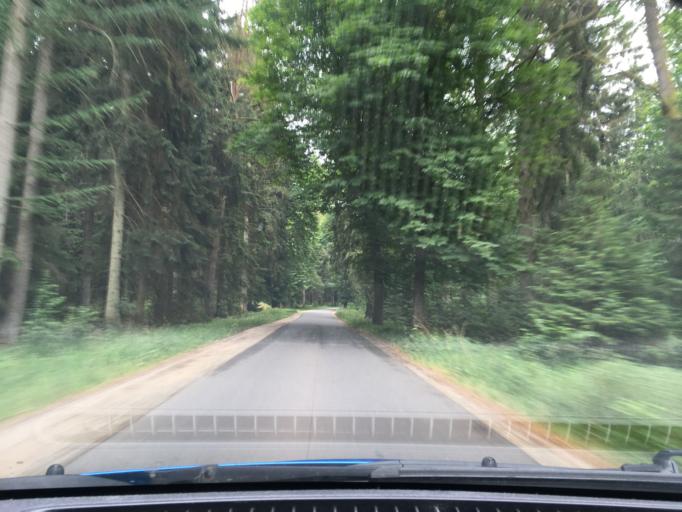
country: DE
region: Lower Saxony
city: Gohrde
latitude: 53.1183
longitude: 10.8630
